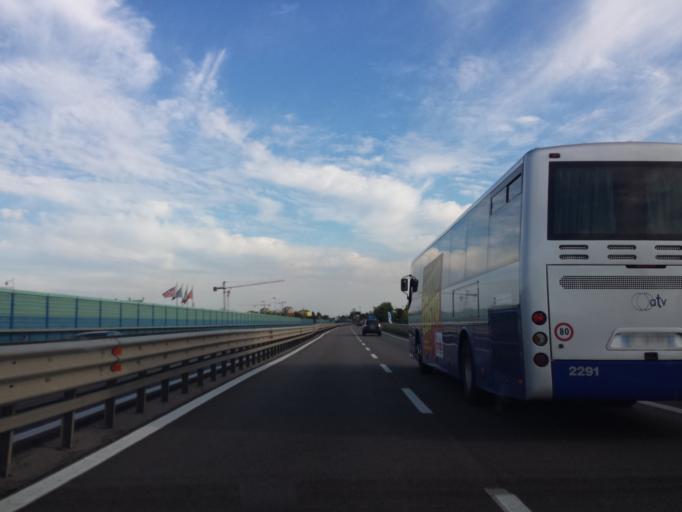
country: IT
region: Veneto
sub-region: Provincia di Verona
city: San Giovanni Lupatoto
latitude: 45.3865
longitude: 11.0265
